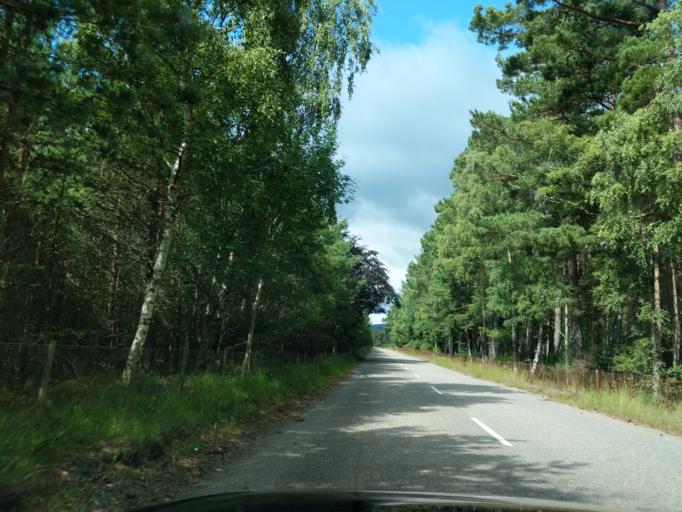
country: GB
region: Scotland
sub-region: Aberdeenshire
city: Aboyne
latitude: 57.0708
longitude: -2.8620
